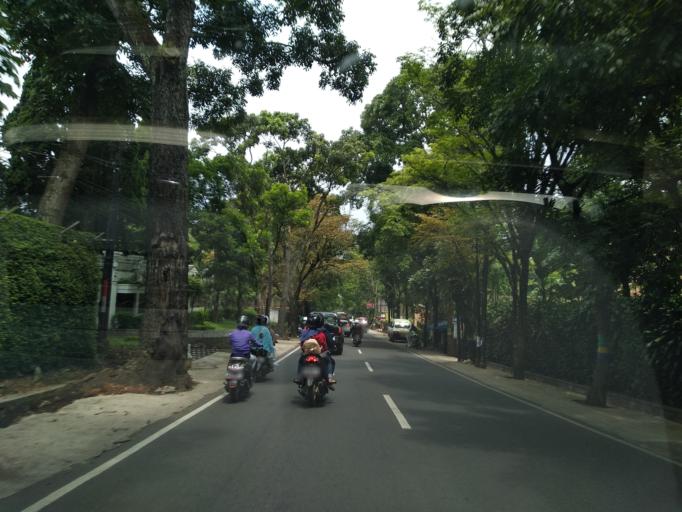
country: ID
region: West Java
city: Lembang
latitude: -6.8522
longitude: 107.5965
